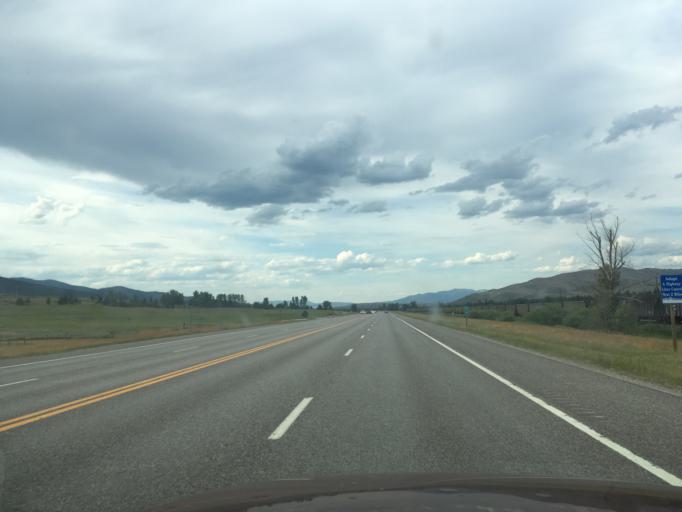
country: US
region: Montana
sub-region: Missoula County
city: Lolo
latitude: 46.6906
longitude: -114.0740
